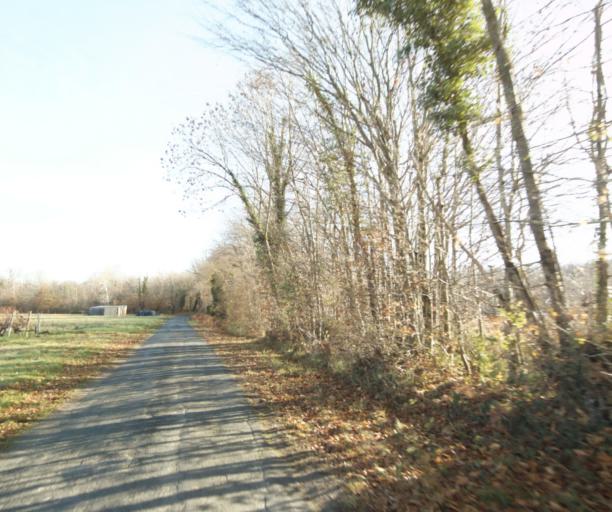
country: FR
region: Poitou-Charentes
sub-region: Departement de la Charente-Maritime
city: Cherac
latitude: 45.7417
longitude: -0.4635
